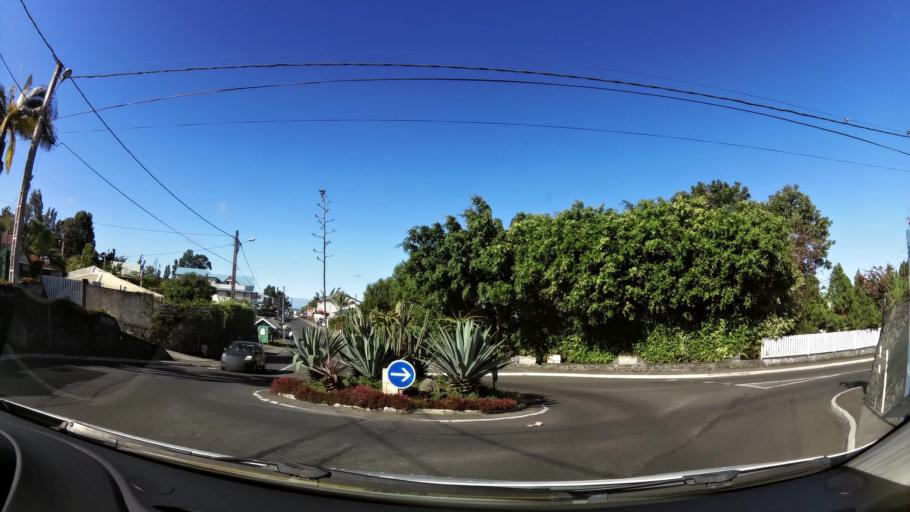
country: RE
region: Reunion
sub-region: Reunion
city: Le Tampon
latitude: -21.2389
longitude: 55.5270
